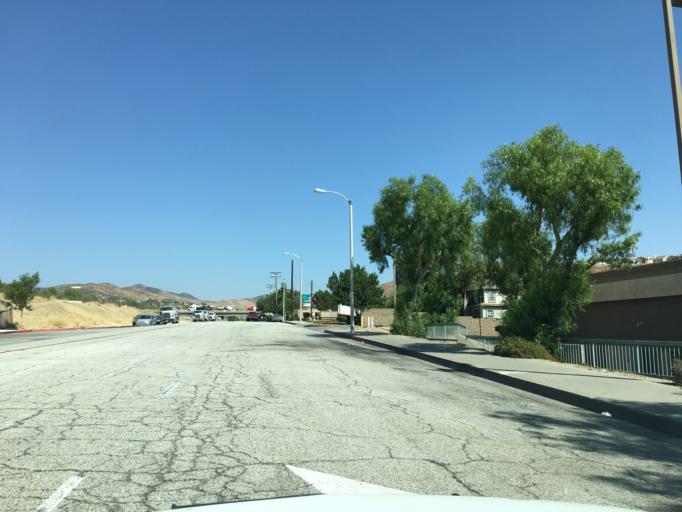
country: US
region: California
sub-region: Los Angeles County
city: Castaic
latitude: 34.4998
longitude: -118.6251
